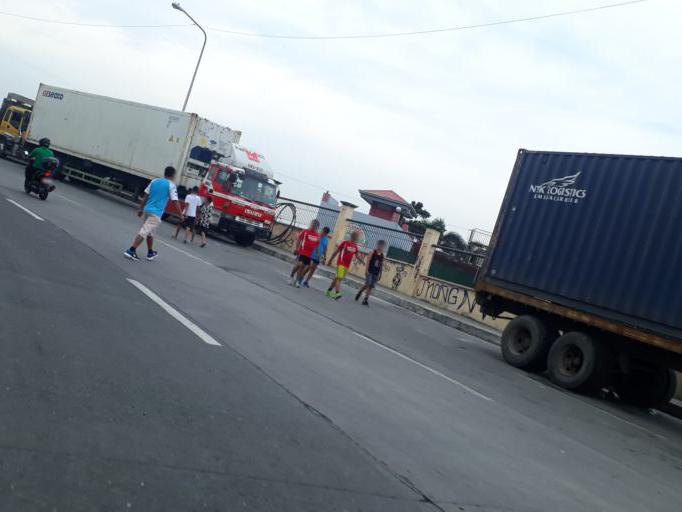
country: PH
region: Metro Manila
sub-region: Caloocan City
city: Niugan
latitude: 14.6513
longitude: 120.9478
